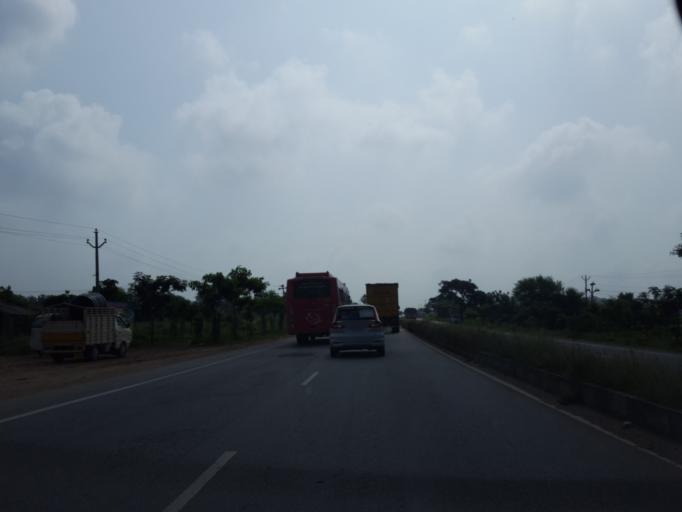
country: IN
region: Telangana
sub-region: Rangareddi
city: Ghatkesar
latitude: 17.2908
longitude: 78.7646
